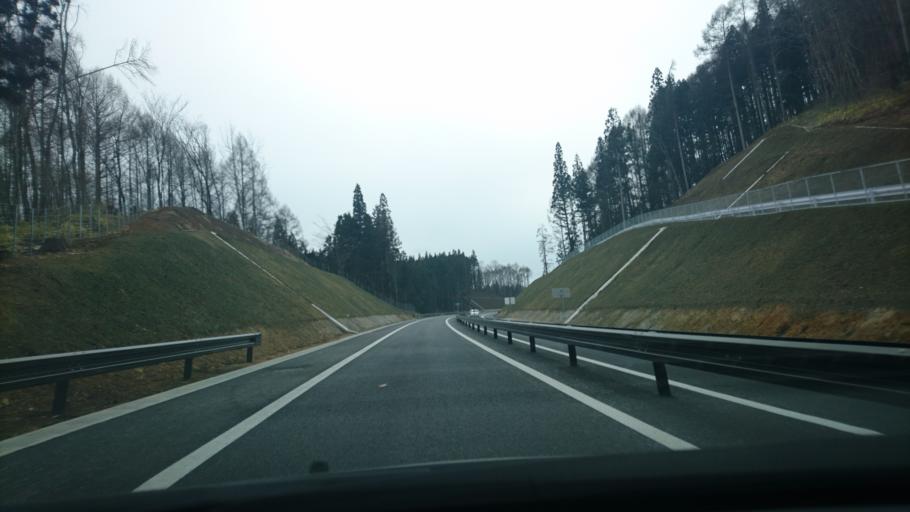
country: JP
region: Iwate
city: Tono
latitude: 39.3145
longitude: 141.5302
